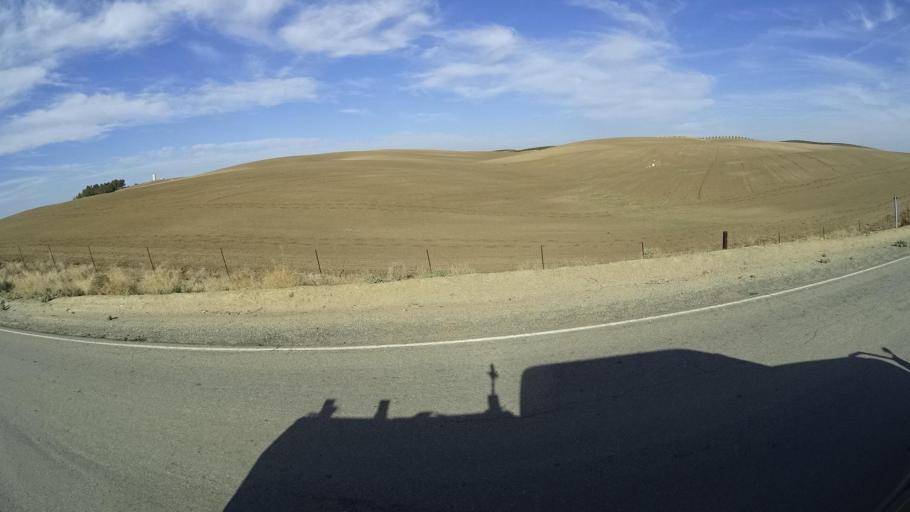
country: US
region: California
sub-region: Kern County
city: McFarland
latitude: 35.6112
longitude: -119.0585
